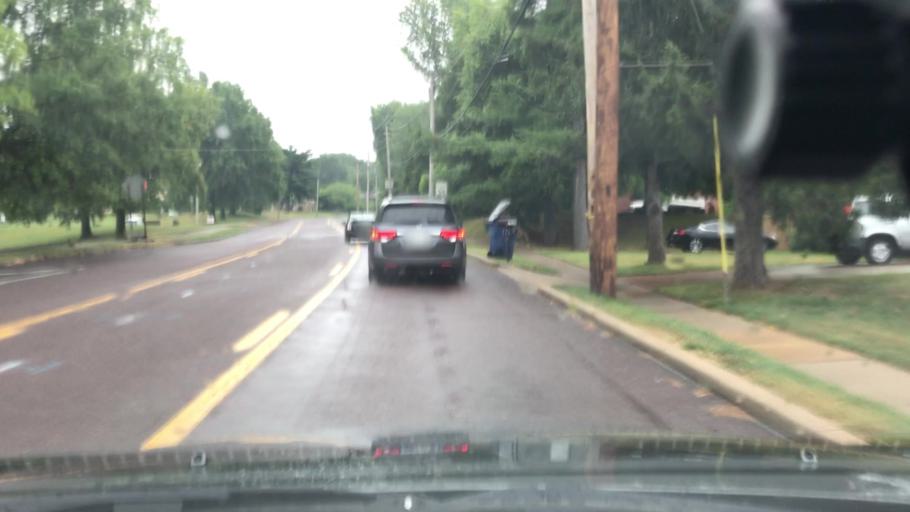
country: US
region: Missouri
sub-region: Saint Louis County
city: Maryland Heights
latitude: 38.6929
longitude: -90.4639
